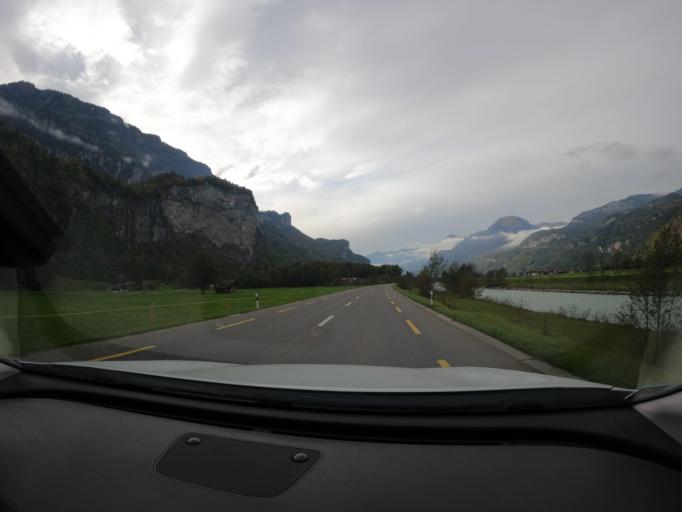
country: CH
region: Bern
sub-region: Interlaken-Oberhasli District
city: Meiringen
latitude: 46.7233
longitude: 8.1794
